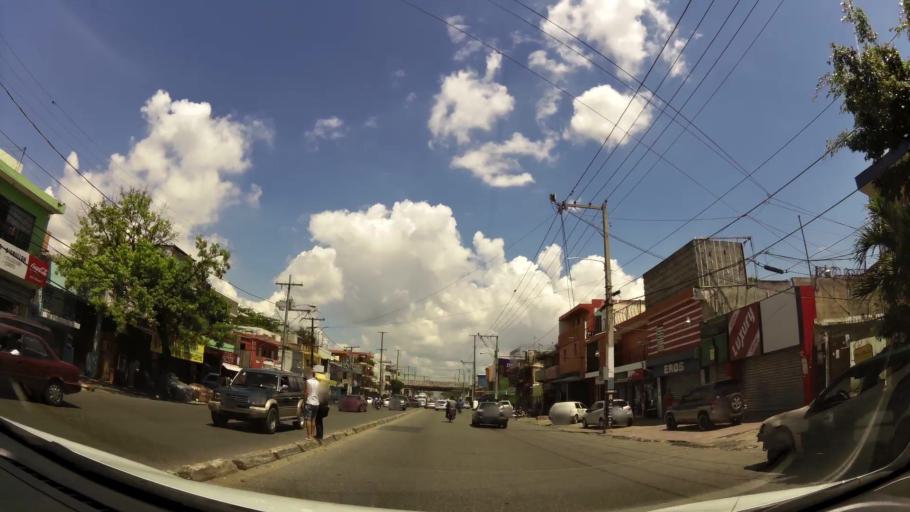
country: DO
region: Nacional
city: Ensanche Luperon
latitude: 18.4989
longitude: -69.8913
